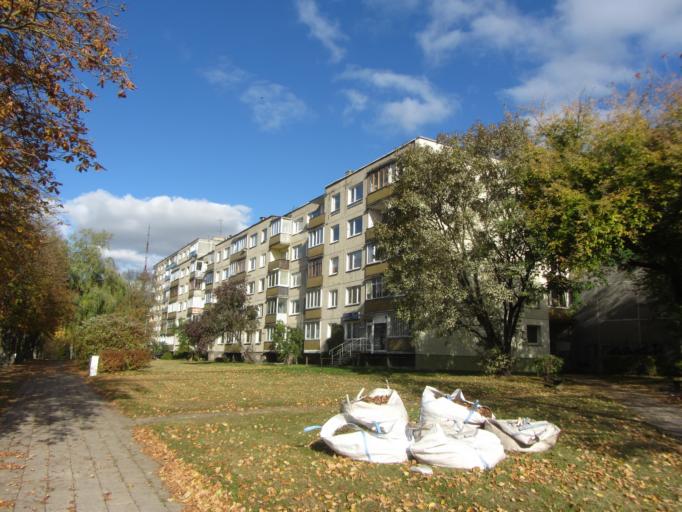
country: LT
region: Vilnius County
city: Lazdynai
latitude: 54.6728
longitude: 25.2100
